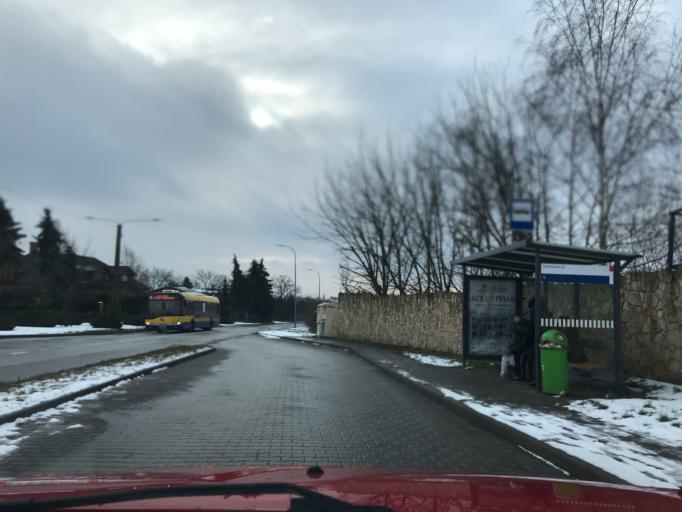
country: PL
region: Greater Poland Voivodeship
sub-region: Kalisz
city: Kalisz
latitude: 51.7774
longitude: 18.1064
